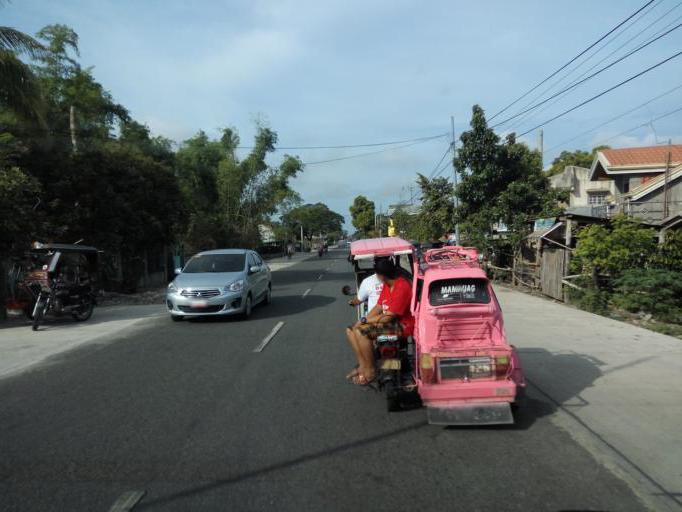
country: PH
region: Cagayan Valley
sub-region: Province of Isabela
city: Cabagan
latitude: 17.4344
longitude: 121.7759
